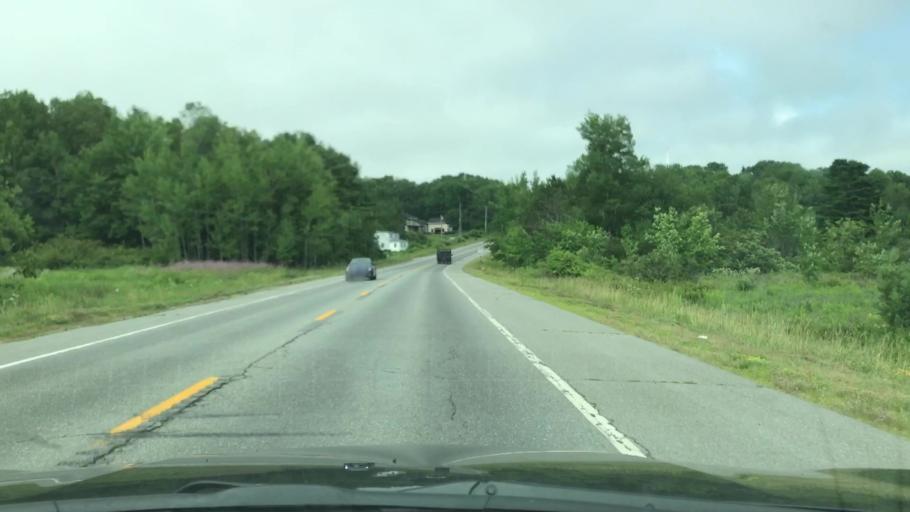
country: US
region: Maine
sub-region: Waldo County
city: Stockton Springs
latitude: 44.4888
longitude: -68.8616
